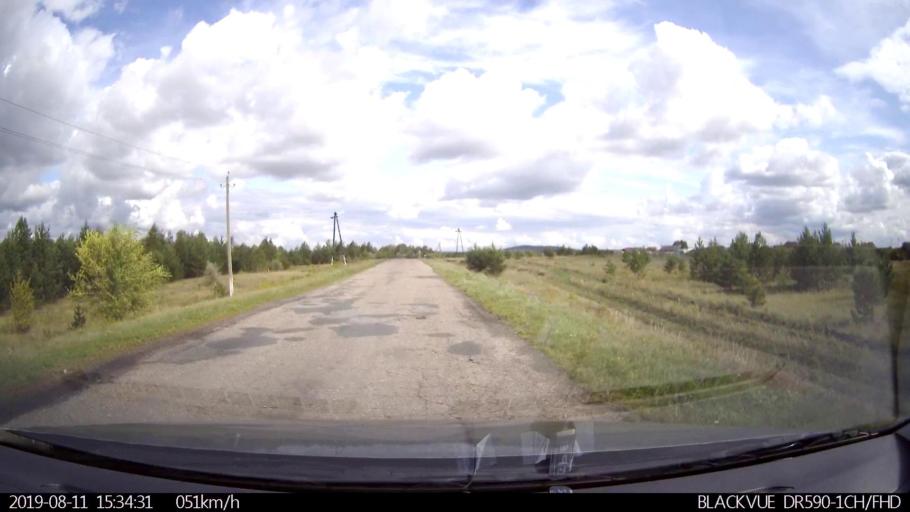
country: RU
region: Ulyanovsk
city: Ignatovka
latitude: 53.8613
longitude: 47.5961
